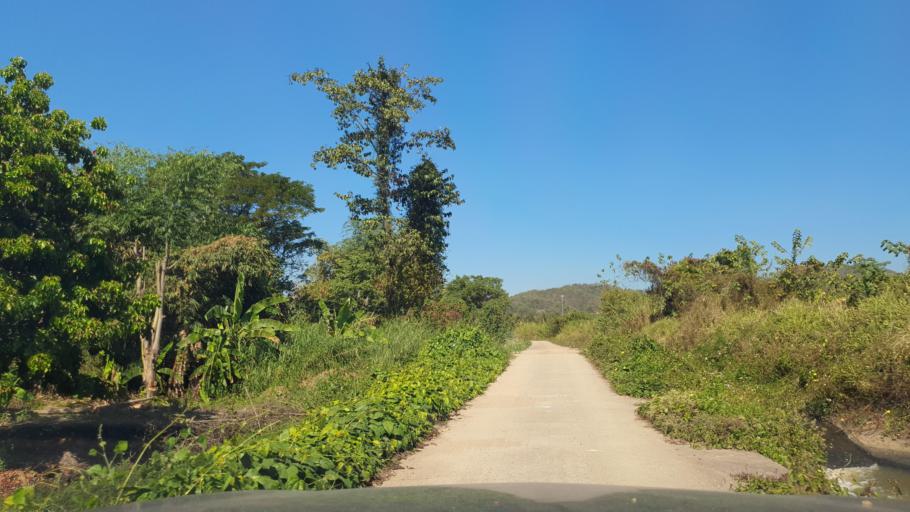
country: TH
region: Chiang Mai
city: San Pa Tong
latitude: 18.6683
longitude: 98.8312
